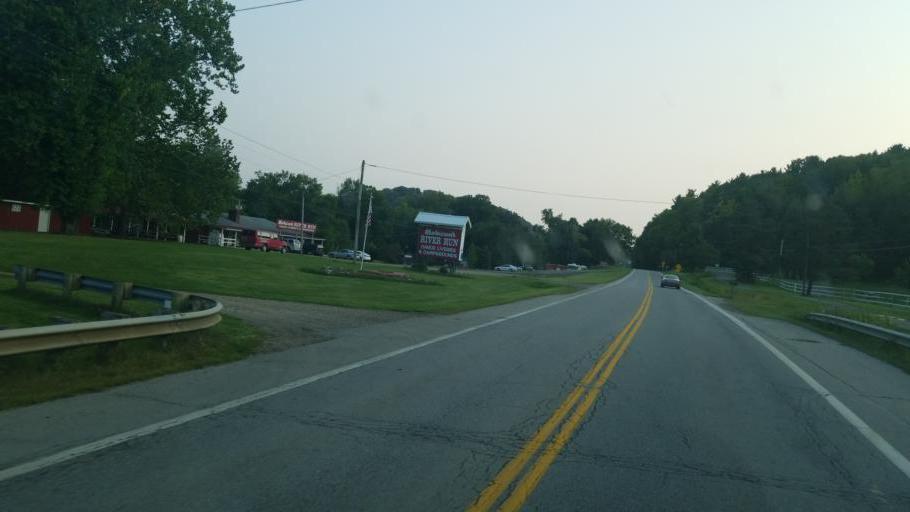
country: US
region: Ohio
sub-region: Ashland County
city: Loudonville
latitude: 40.6162
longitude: -82.2539
